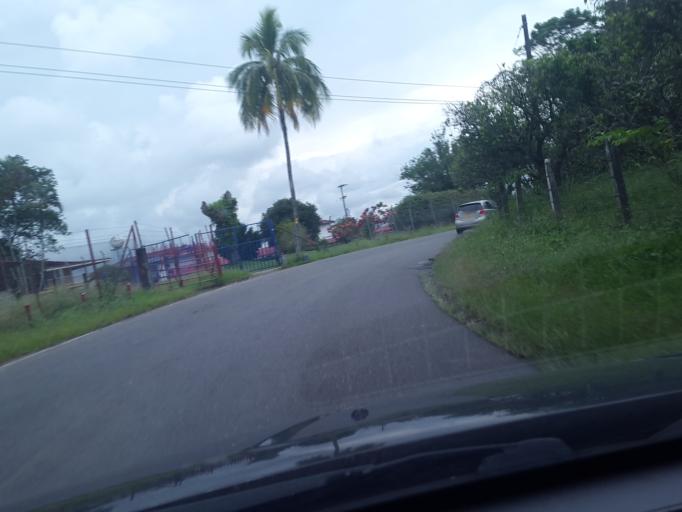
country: CO
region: Quindio
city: La Tebaida
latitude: 4.4925
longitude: -75.7934
